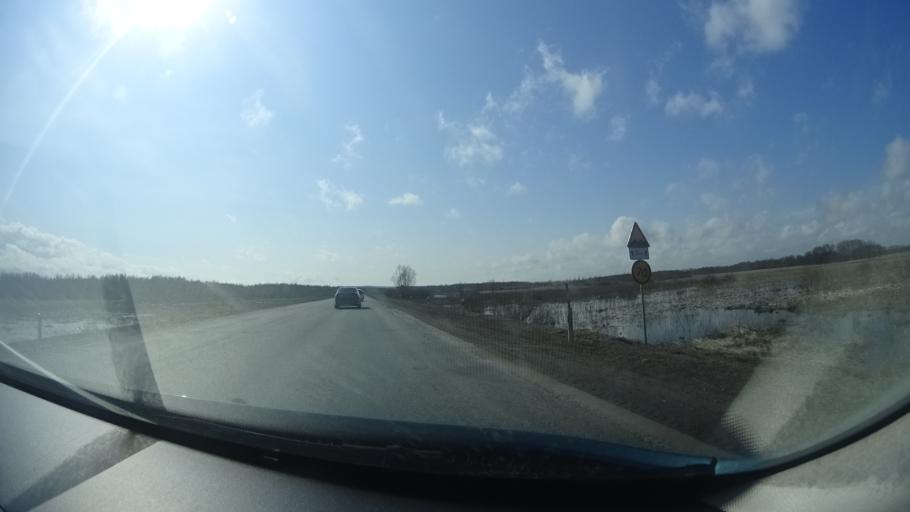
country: RU
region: Bashkortostan
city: Mikhaylovka
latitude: 54.9206
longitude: 55.7364
